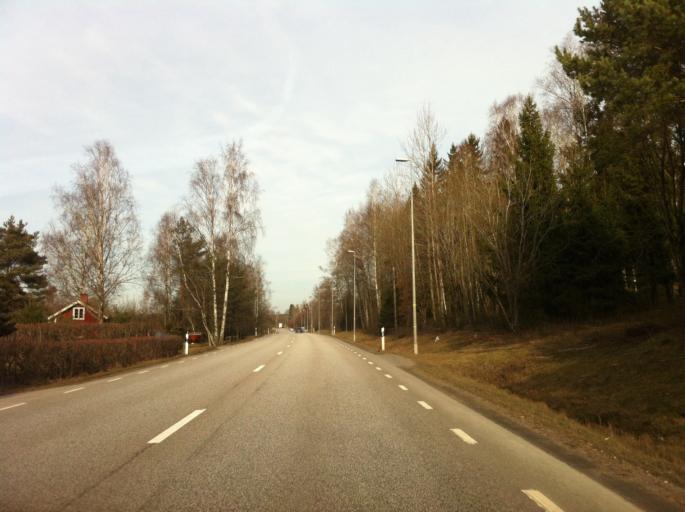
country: SE
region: Vaestra Goetaland
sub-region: Gullspangs Kommun
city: Gullspang
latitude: 58.9758
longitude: 14.0797
